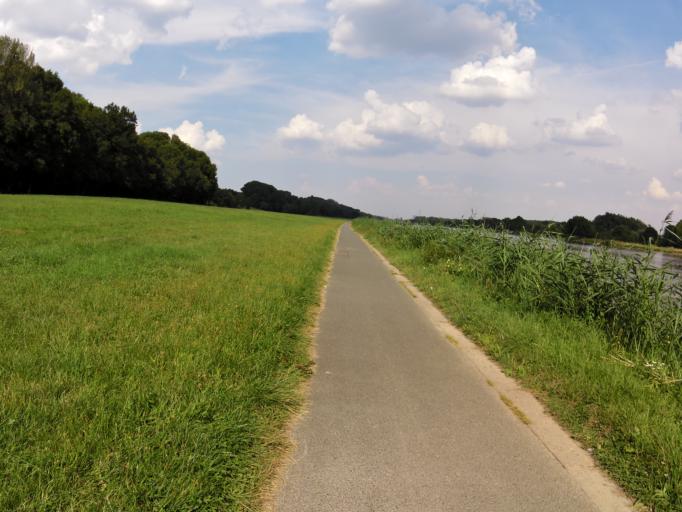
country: DE
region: North Rhine-Westphalia
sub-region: Regierungsbezirk Detmold
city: Minden
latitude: 52.3287
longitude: 8.9289
